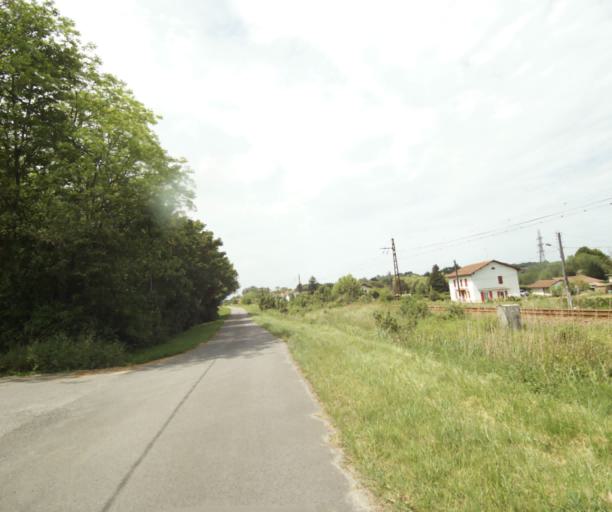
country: FR
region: Aquitaine
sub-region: Departement des Pyrenees-Atlantiques
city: Mouguerre
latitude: 43.4840
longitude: -1.4327
